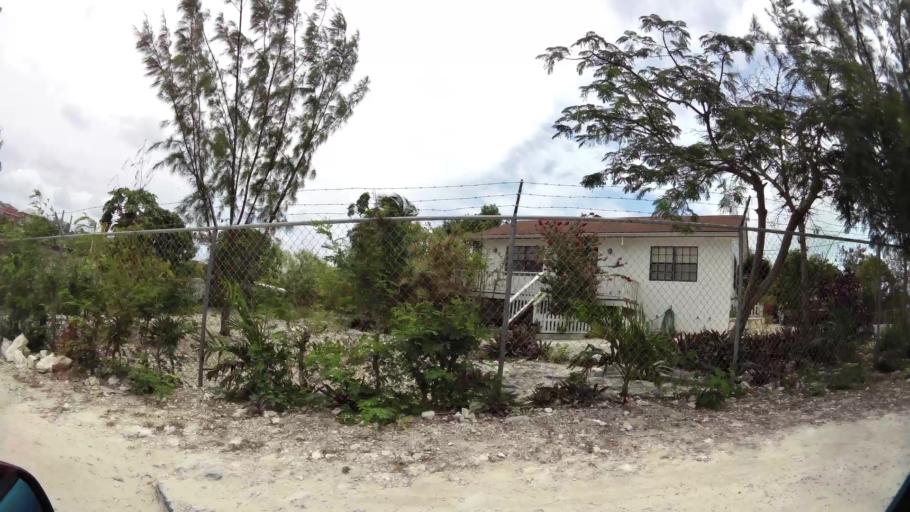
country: BS
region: Mayaguana
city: Abraham's Bay
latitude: 21.7850
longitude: -72.2586
